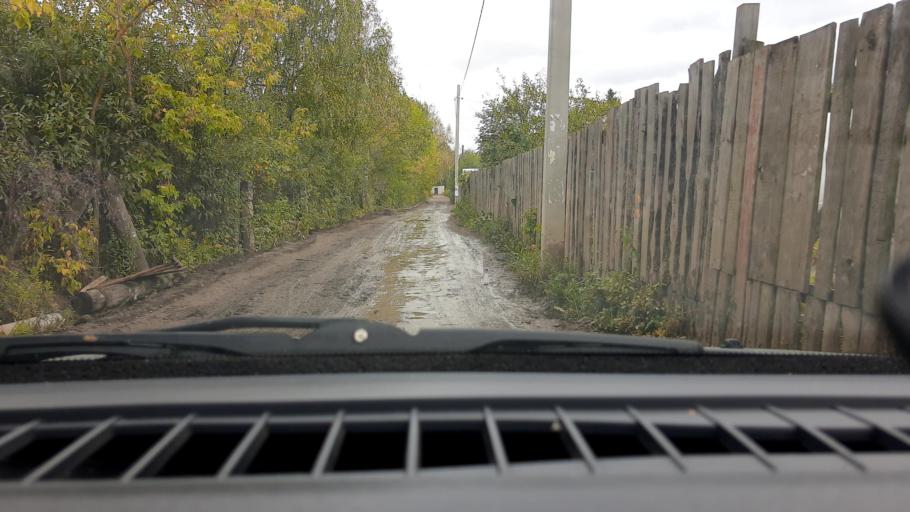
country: RU
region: Nizjnij Novgorod
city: Gorbatovka
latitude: 56.3239
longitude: 43.8382
